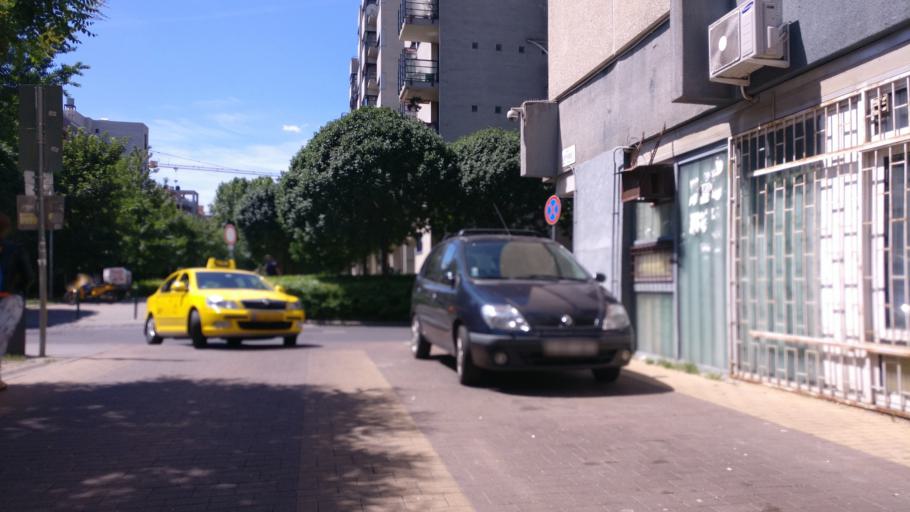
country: HU
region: Budapest
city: Budapest III. keruelet
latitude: 47.5298
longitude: 19.0589
